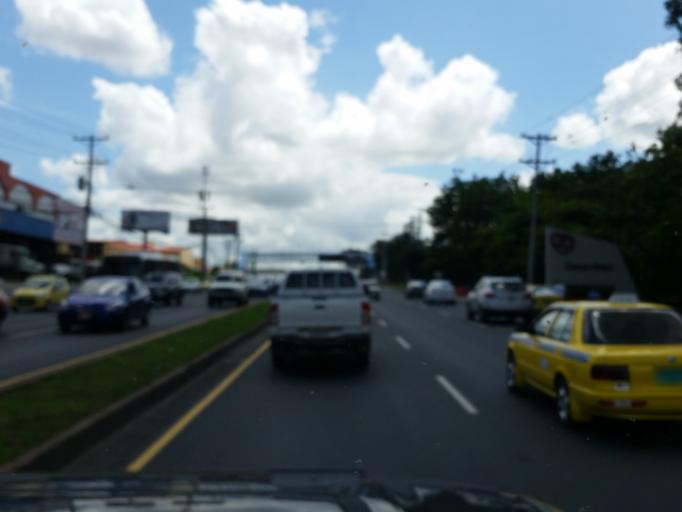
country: PA
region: Panama
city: San Miguelito
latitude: 9.0513
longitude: -79.4468
